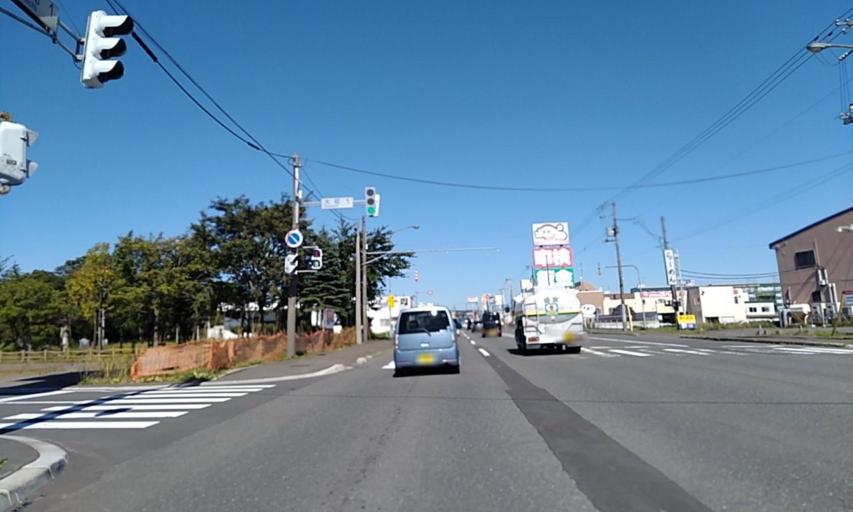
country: JP
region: Hokkaido
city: Kitahiroshima
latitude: 42.8889
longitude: 141.5696
